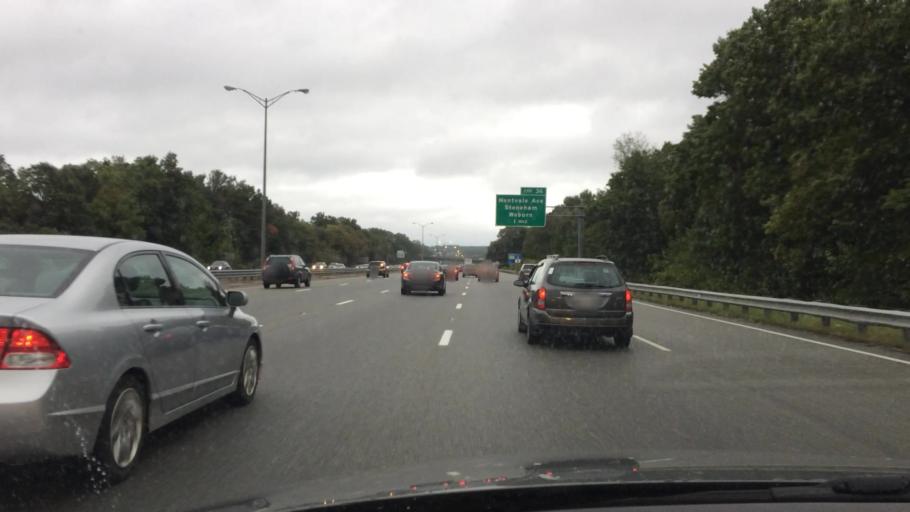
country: US
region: Massachusetts
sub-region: Middlesex County
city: Stoneham
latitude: 42.4970
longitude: -71.1183
